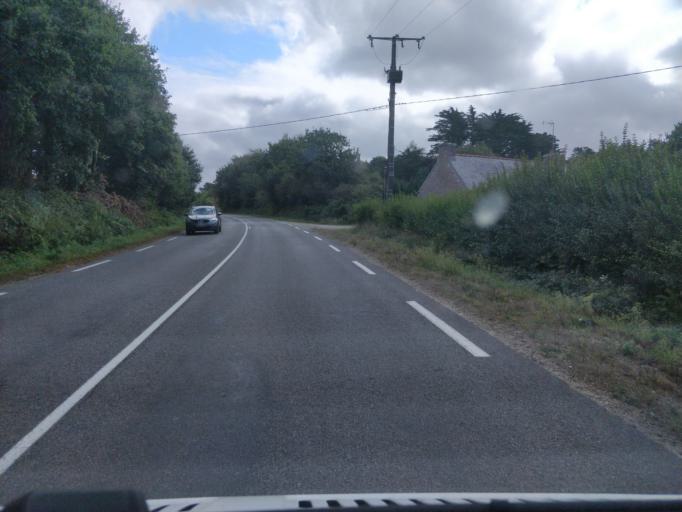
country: FR
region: Brittany
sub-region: Departement du Finistere
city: Plogastel-Saint-Germain
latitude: 47.9952
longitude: -4.2487
